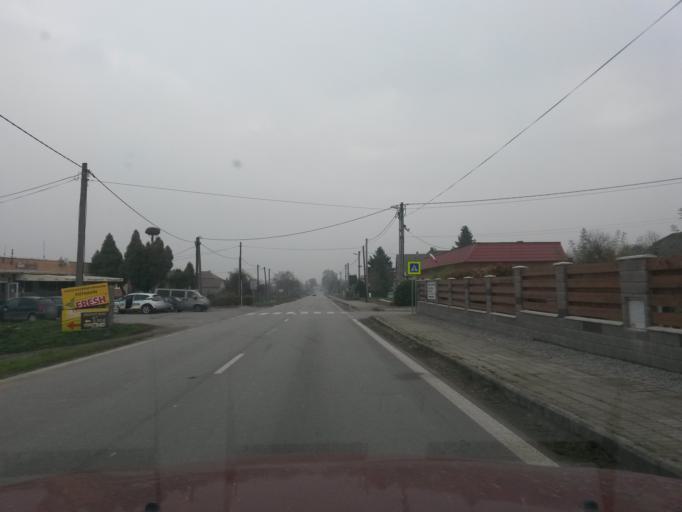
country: SK
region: Kosicky
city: Kosice
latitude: 48.8358
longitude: 21.2861
